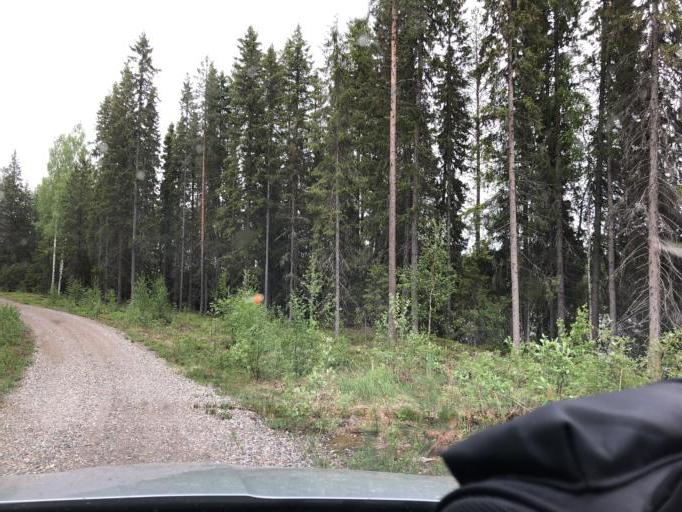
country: SE
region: Norrbotten
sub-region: Pitea Kommun
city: Roknas
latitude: 65.3999
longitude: 21.2688
